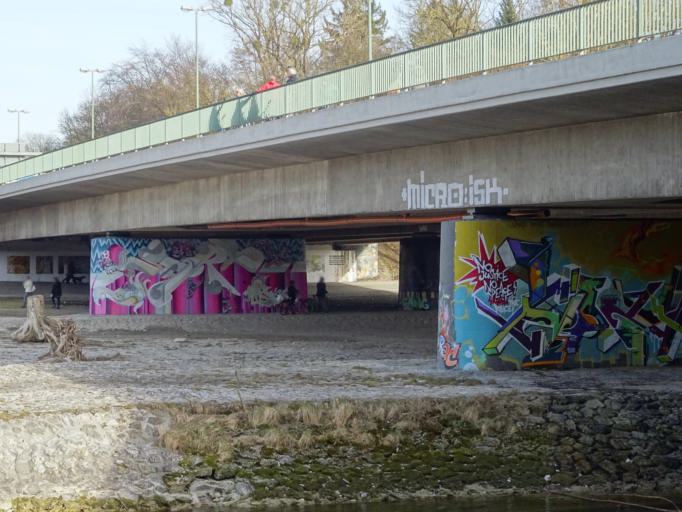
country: DE
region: Bavaria
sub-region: Upper Bavaria
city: Munich
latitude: 48.1132
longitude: 11.5589
